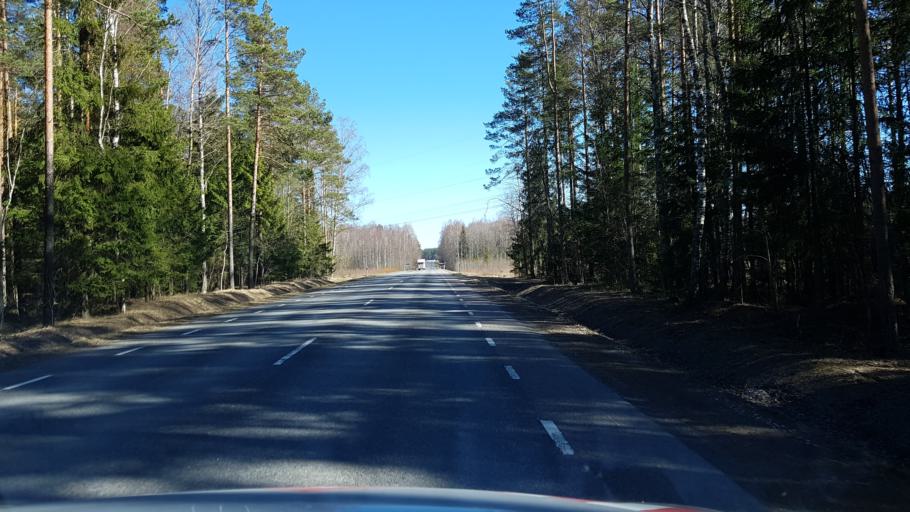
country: EE
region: Laeaene-Virumaa
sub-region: Viru-Nigula vald
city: Kunda
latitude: 59.3669
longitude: 26.6035
